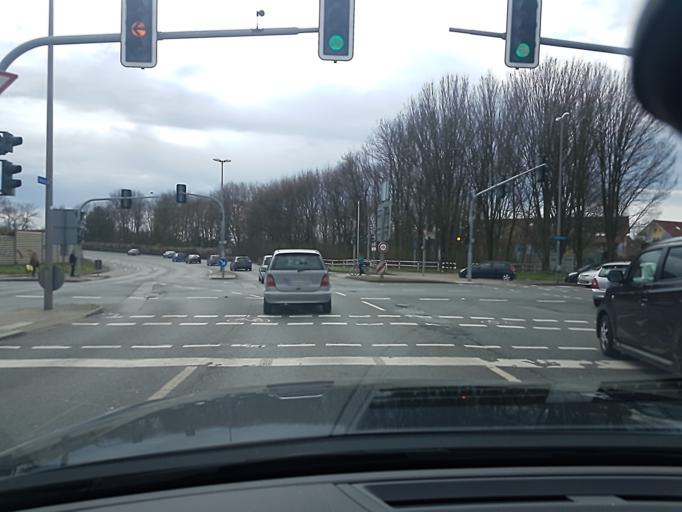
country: DE
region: North Rhine-Westphalia
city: Kamen
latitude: 51.5924
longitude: 7.6538
